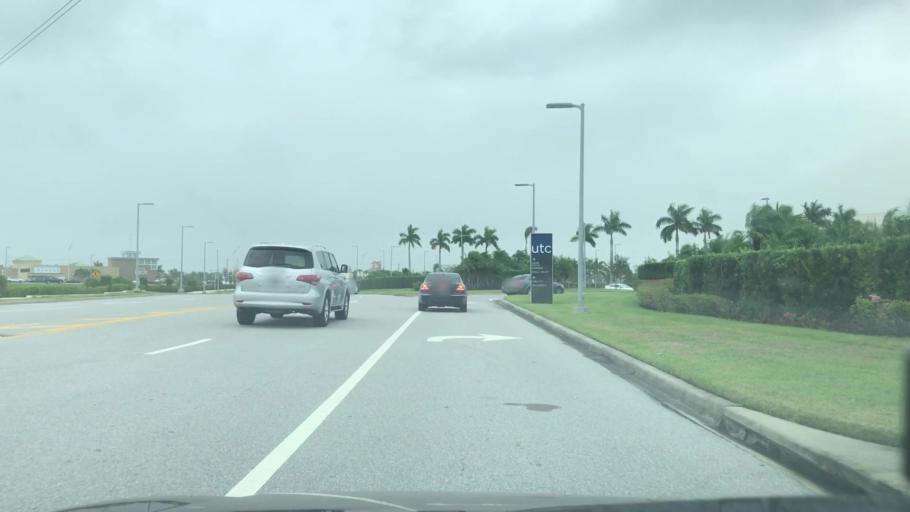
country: US
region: Florida
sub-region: Sarasota County
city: The Meadows
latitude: 27.3864
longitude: -82.4550
